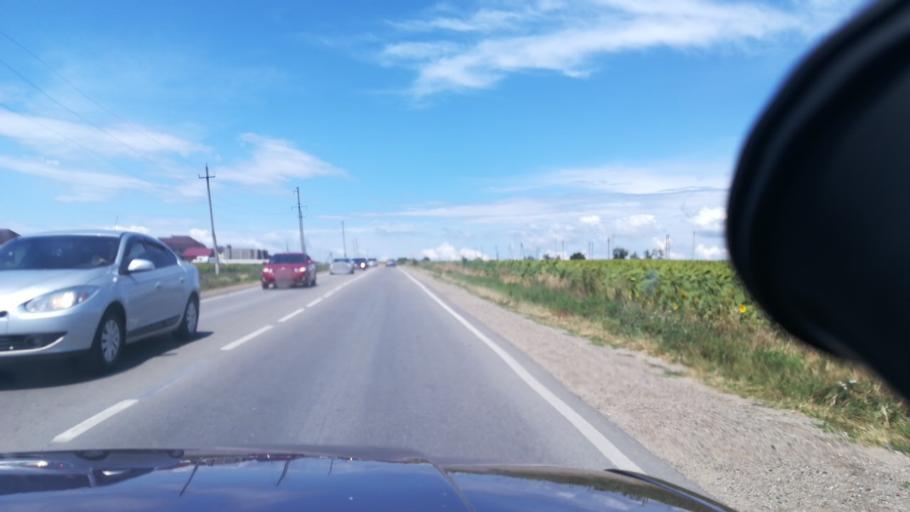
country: RU
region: Krasnodarskiy
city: Tsibanobalka
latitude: 44.9606
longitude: 37.3046
